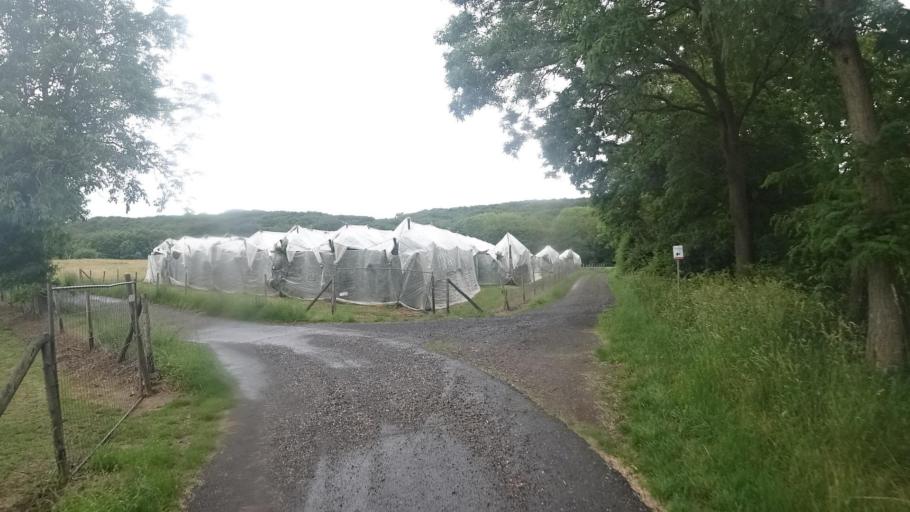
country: DE
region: Rheinland-Pfalz
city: Bad Neuenahr-Ahrweiler
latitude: 50.5546
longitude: 7.0957
